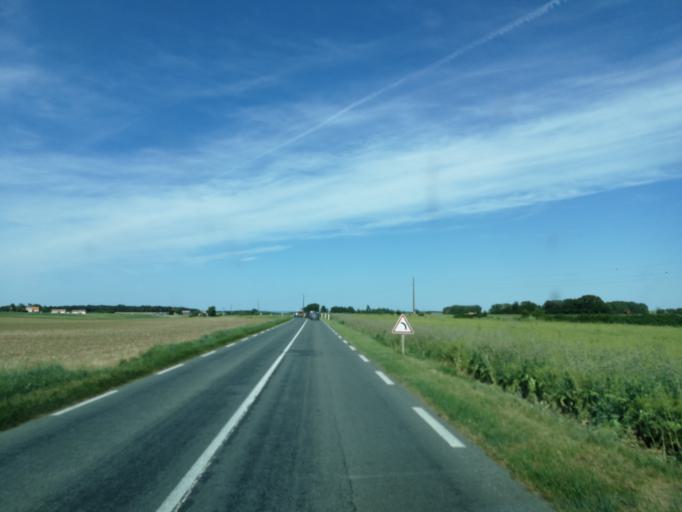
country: FR
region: Poitou-Charentes
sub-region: Departement de la Vienne
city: Loudun
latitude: 47.0292
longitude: 0.1167
